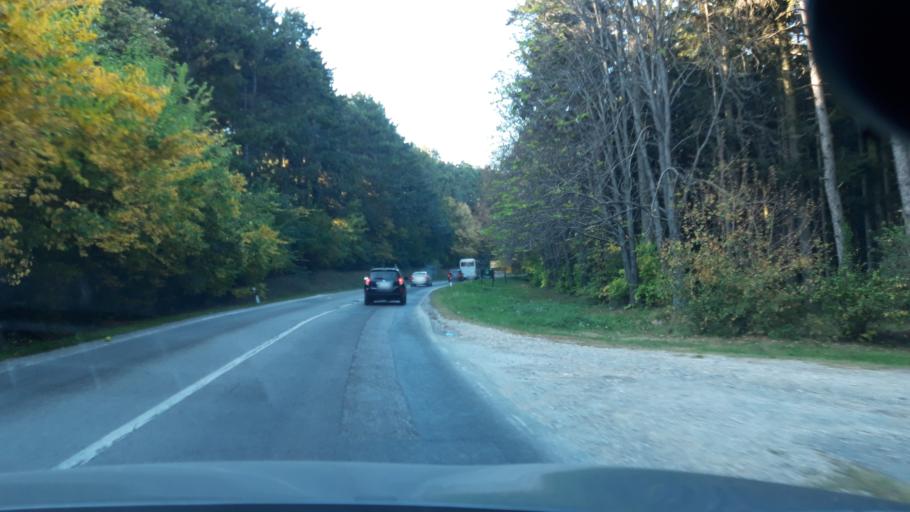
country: RS
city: Vrdnik
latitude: 45.1472
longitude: 19.8300
